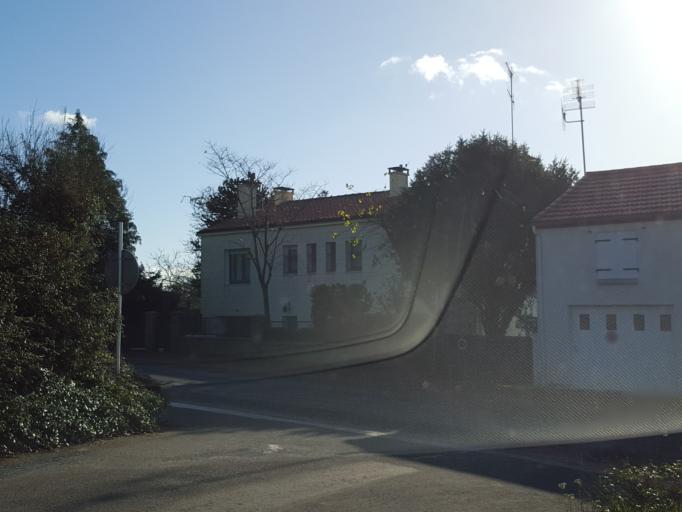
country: FR
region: Pays de la Loire
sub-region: Departement de la Vendee
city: Venansault
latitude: 46.6846
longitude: -1.5101
